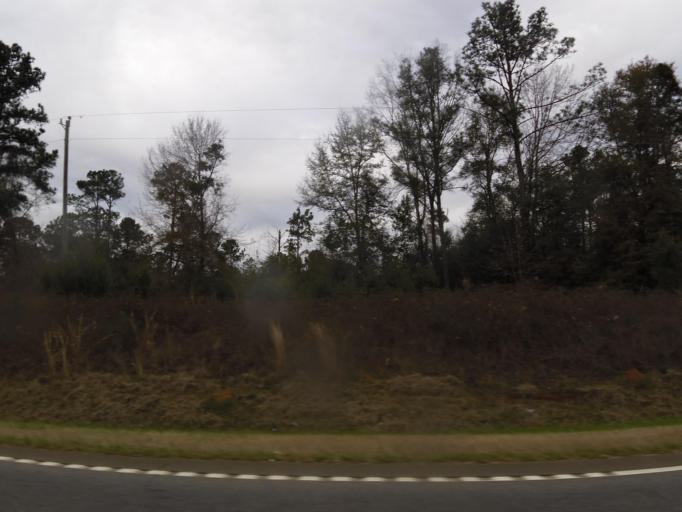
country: US
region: Georgia
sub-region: Randolph County
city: Shellman
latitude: 31.7755
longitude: -84.6951
